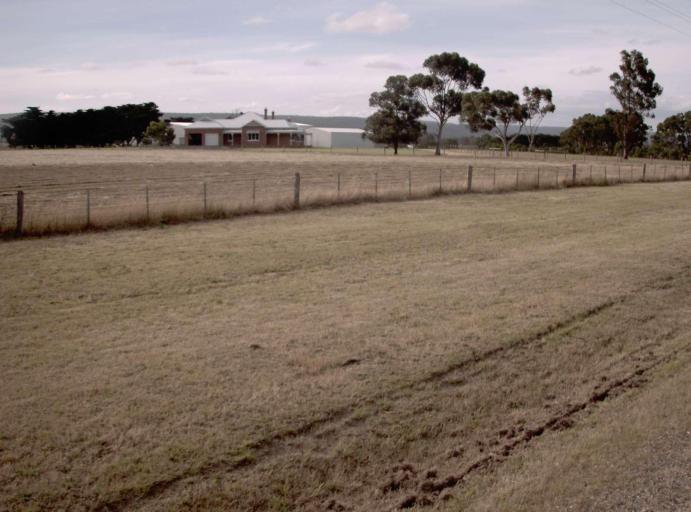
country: AU
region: Victoria
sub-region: Wellington
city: Heyfield
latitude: -38.0512
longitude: 146.6637
